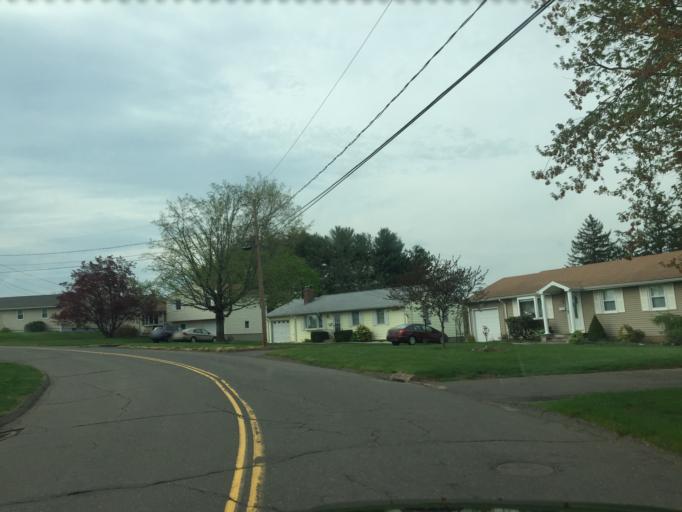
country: US
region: Connecticut
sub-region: Hartford County
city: Newington
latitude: 41.6987
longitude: -72.7402
